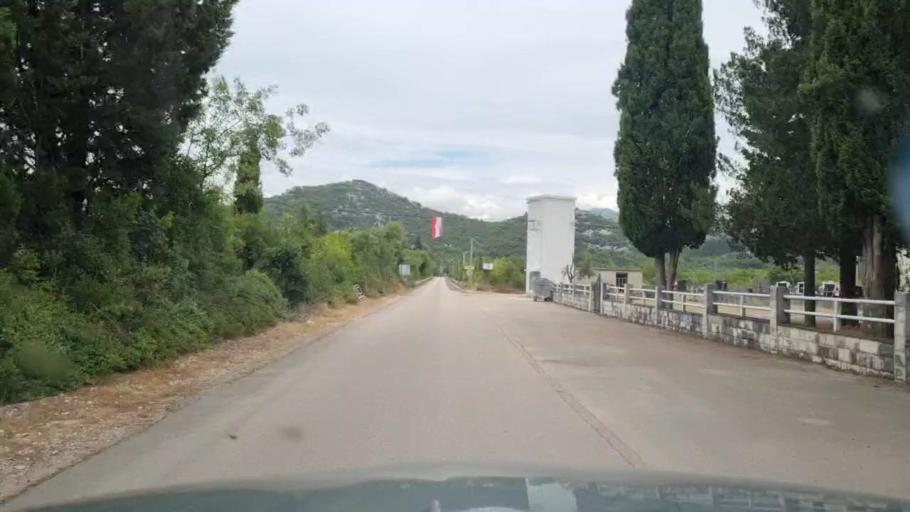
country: BA
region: Federation of Bosnia and Herzegovina
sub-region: Hercegovacko-Bosanski Kanton
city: Neum
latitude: 42.9144
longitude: 17.6656
